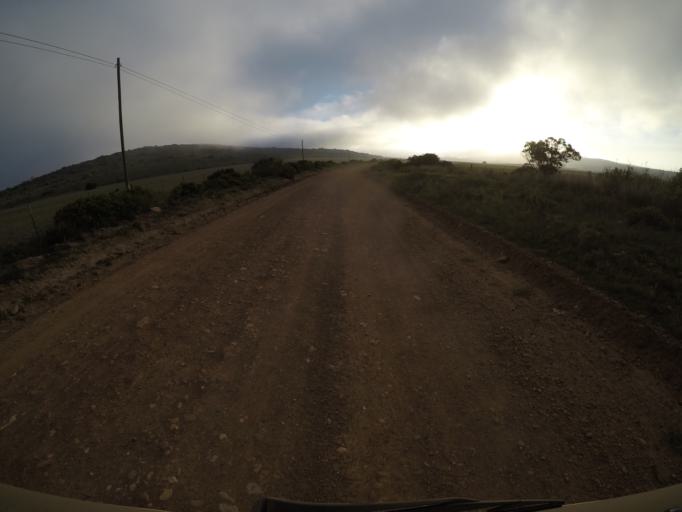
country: ZA
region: Western Cape
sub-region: Eden District Municipality
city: Mossel Bay
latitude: -34.1419
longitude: 22.0354
